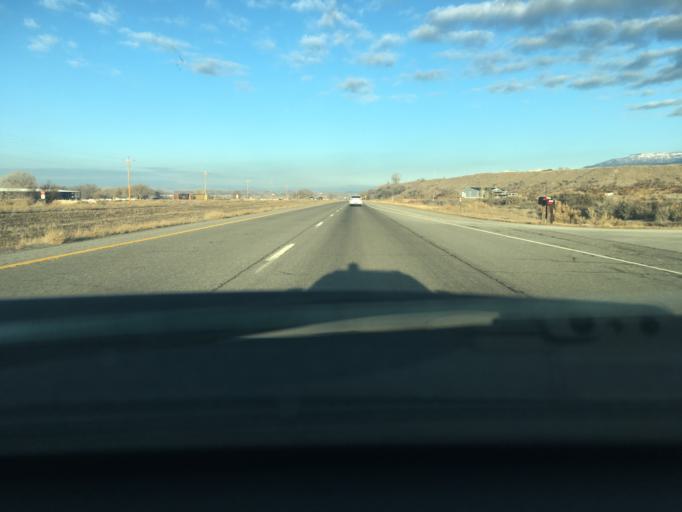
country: US
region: Colorado
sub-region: Delta County
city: Delta
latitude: 38.7026
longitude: -108.0350
